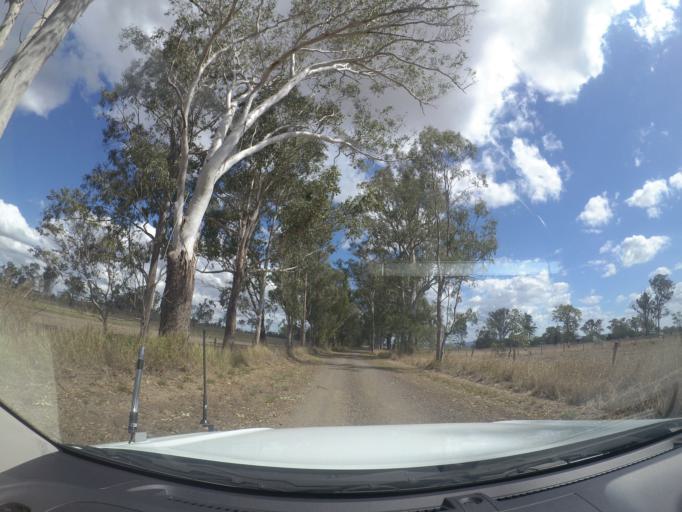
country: AU
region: Queensland
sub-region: Logan
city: Cedar Vale
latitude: -27.8833
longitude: 152.9609
